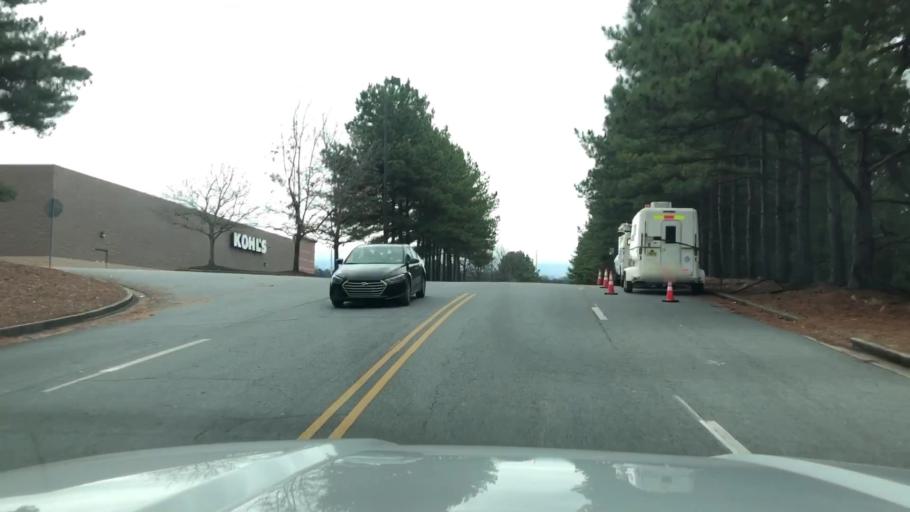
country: US
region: Georgia
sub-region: Cherokee County
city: Woodstock
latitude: 34.0819
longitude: -84.5442
